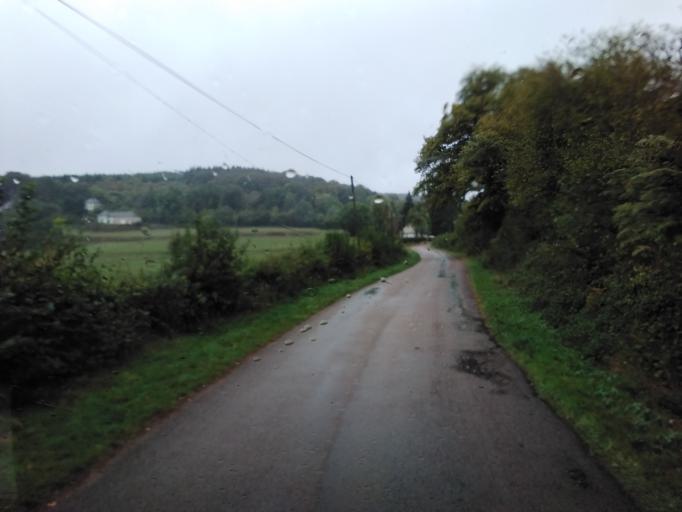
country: FR
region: Bourgogne
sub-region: Departement de la Nievre
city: Lormes
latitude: 47.2922
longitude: 3.9718
